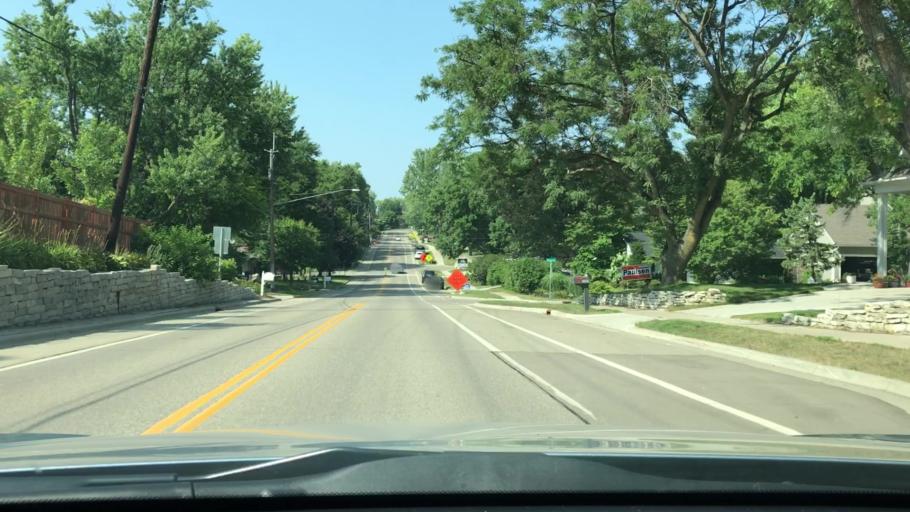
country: US
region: Minnesota
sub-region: Hennepin County
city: Edina
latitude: 44.8984
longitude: -93.3679
